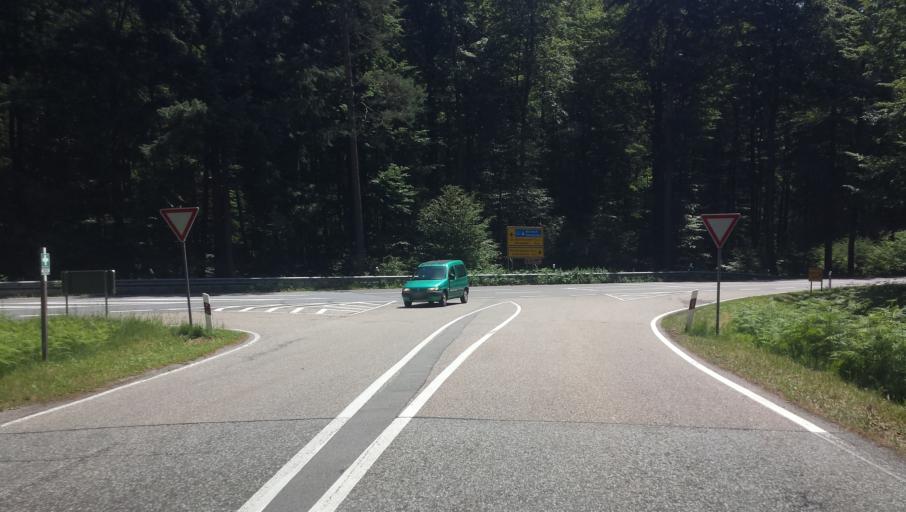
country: DE
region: Rheinland-Pfalz
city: Trippstadt
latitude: 49.3542
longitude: 7.8313
